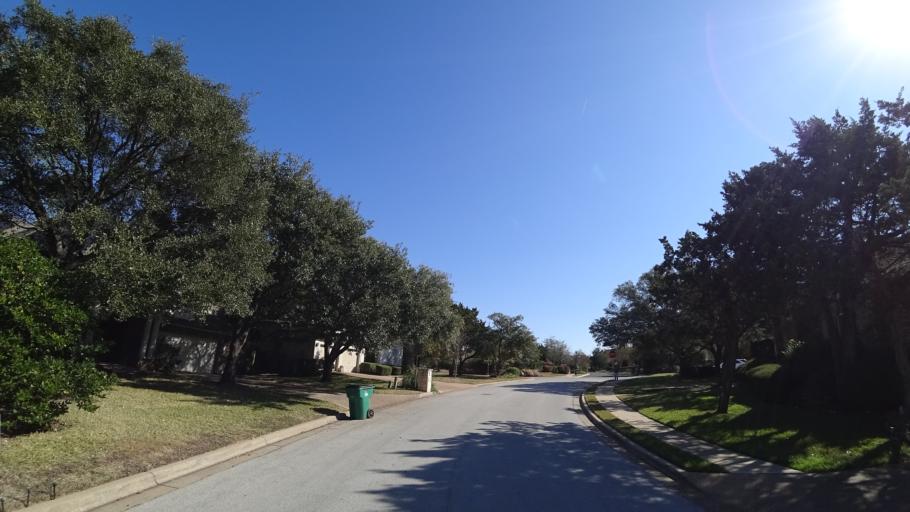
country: US
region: Texas
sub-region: Travis County
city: Hudson Bend
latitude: 30.3820
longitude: -97.8522
